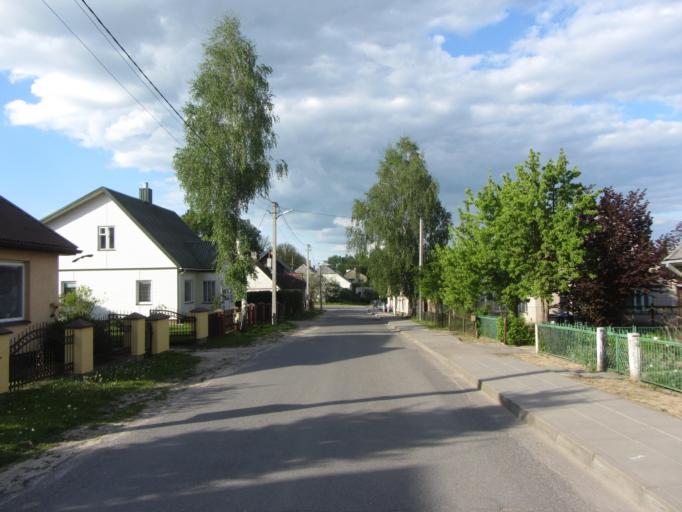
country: LT
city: Sirvintos
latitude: 55.0459
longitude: 24.9495
